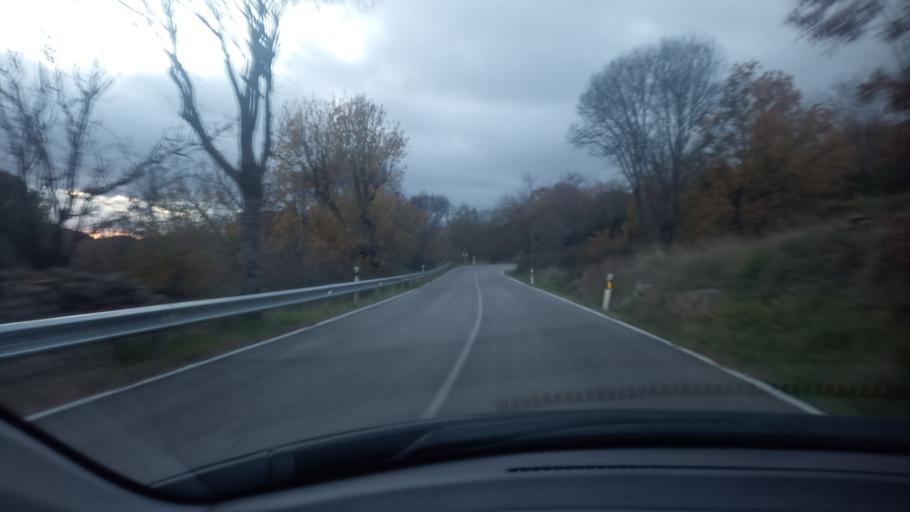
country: ES
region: Madrid
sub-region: Provincia de Madrid
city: Zarzalejo
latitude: 40.5463
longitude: -4.1744
